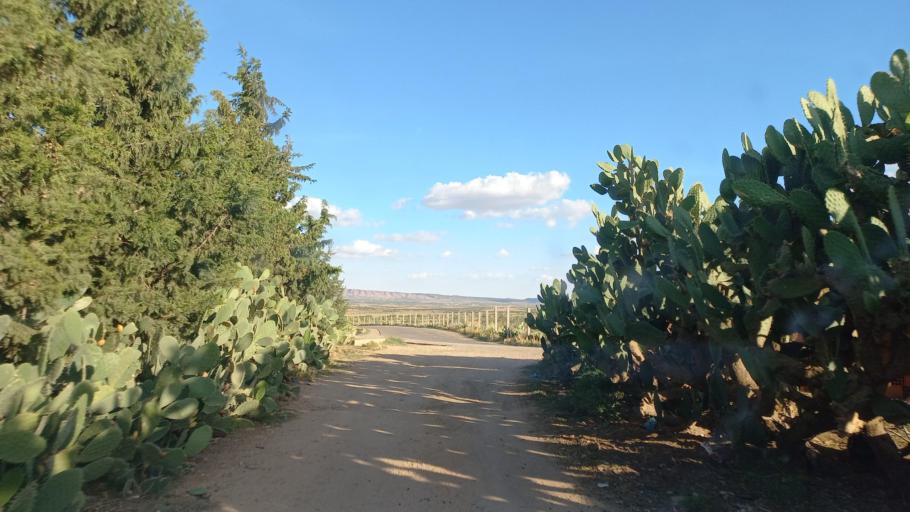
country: TN
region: Al Qasrayn
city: Sbiba
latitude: 35.3795
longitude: 9.0226
